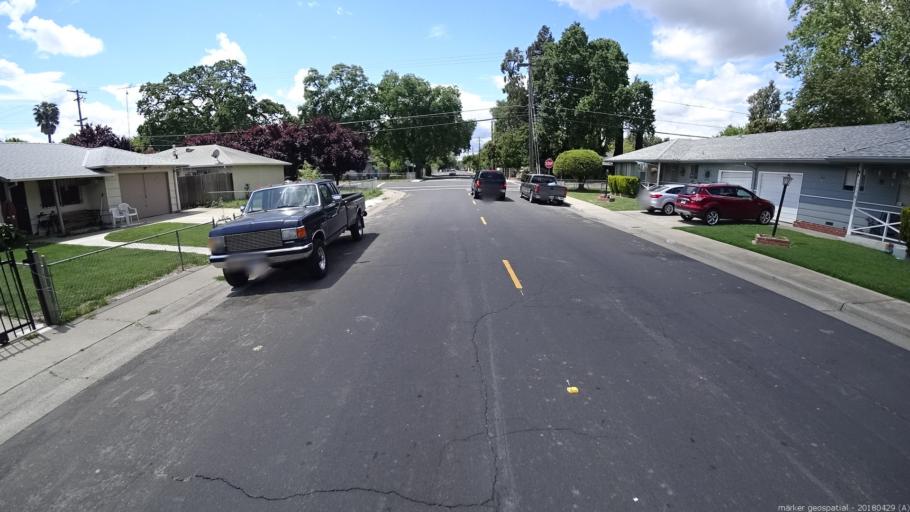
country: US
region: California
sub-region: Yolo County
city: West Sacramento
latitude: 38.5957
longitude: -121.5385
